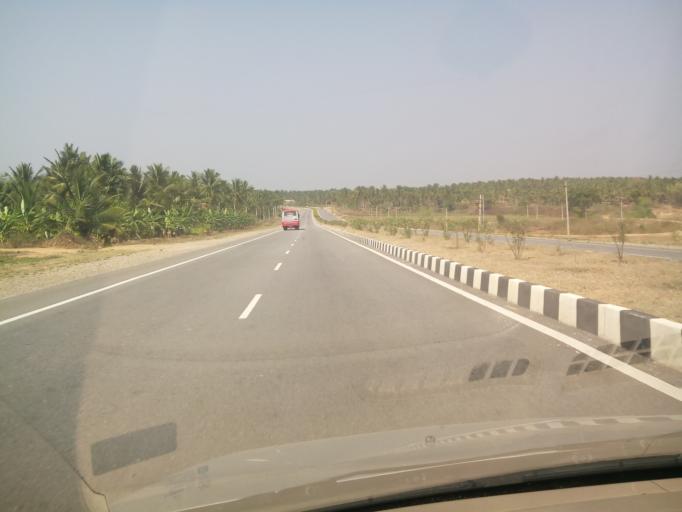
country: IN
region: Karnataka
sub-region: Hassan
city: Shravanabelagola
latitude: 12.9167
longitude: 76.4628
